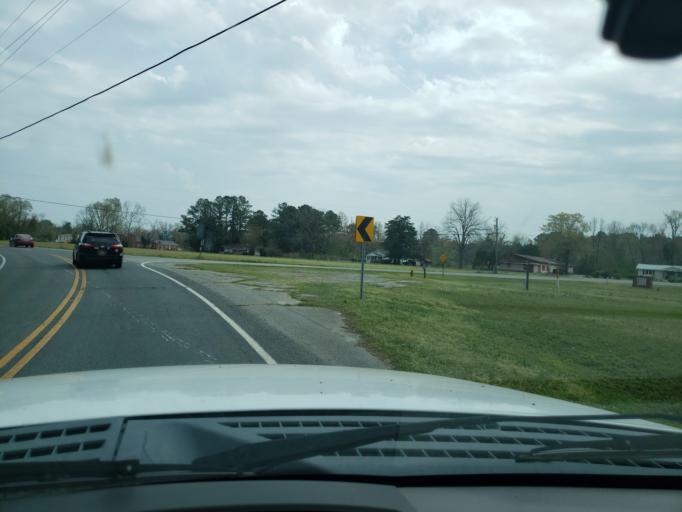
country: US
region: North Carolina
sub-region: Duplin County
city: Beulaville
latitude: 34.7809
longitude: -77.8356
